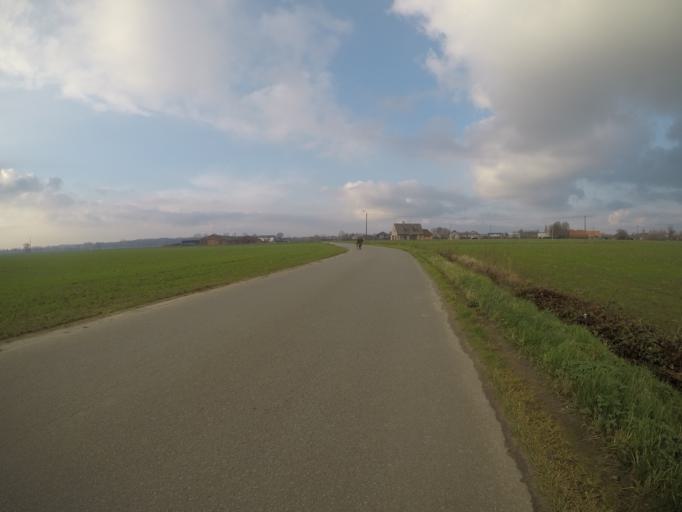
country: BE
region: Flanders
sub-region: Provincie West-Vlaanderen
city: Lichtervelde
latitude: 51.0692
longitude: 3.1696
